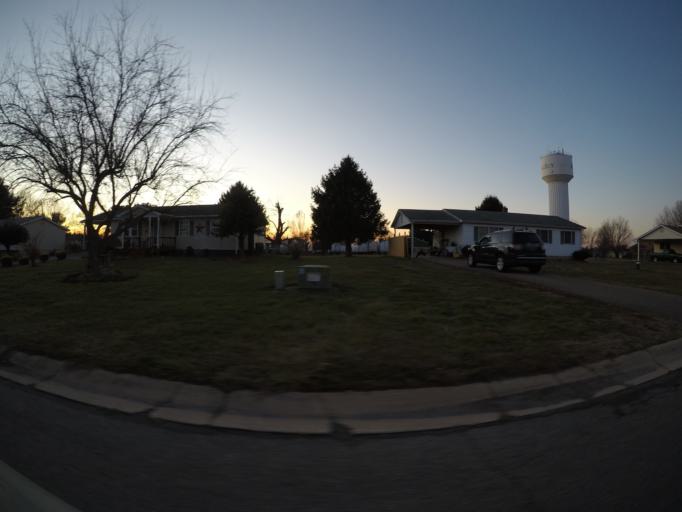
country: US
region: Maryland
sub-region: Cecil County
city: Rising Sun
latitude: 39.6939
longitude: -76.0560
